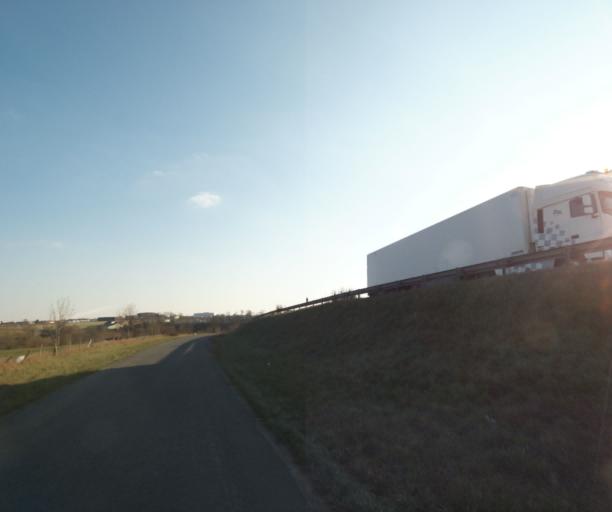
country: FR
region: Poitou-Charentes
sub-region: Departement des Deux-Sevres
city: Aiffres
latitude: 46.3263
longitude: -0.4130
